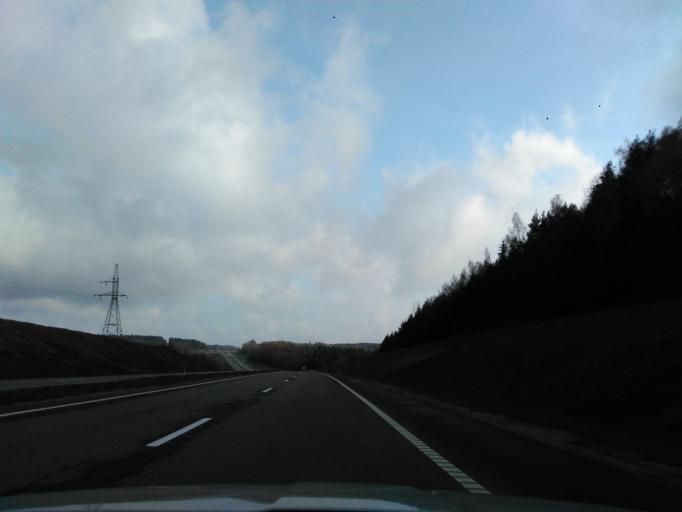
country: BY
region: Minsk
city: Lahoysk
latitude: 54.1927
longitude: 27.8157
